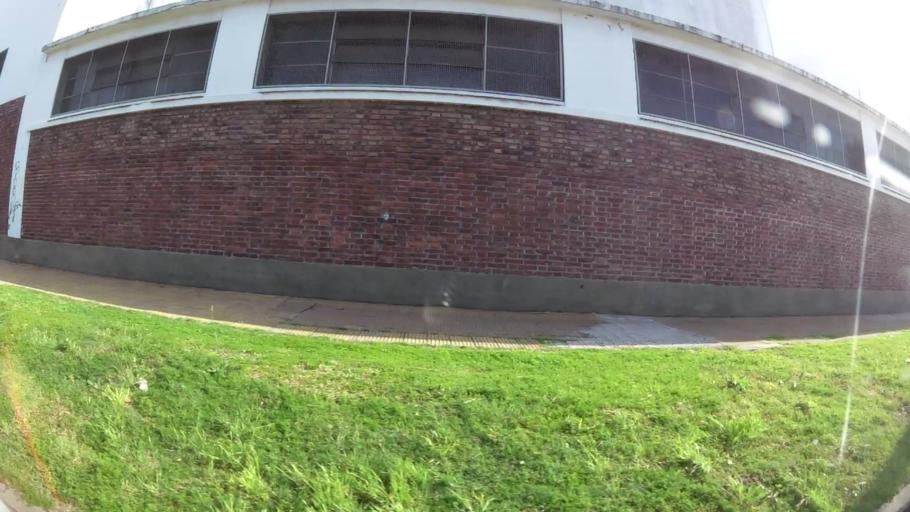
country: AR
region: Buenos Aires
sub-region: Partido de Merlo
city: Merlo
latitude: -34.6612
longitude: -58.7373
